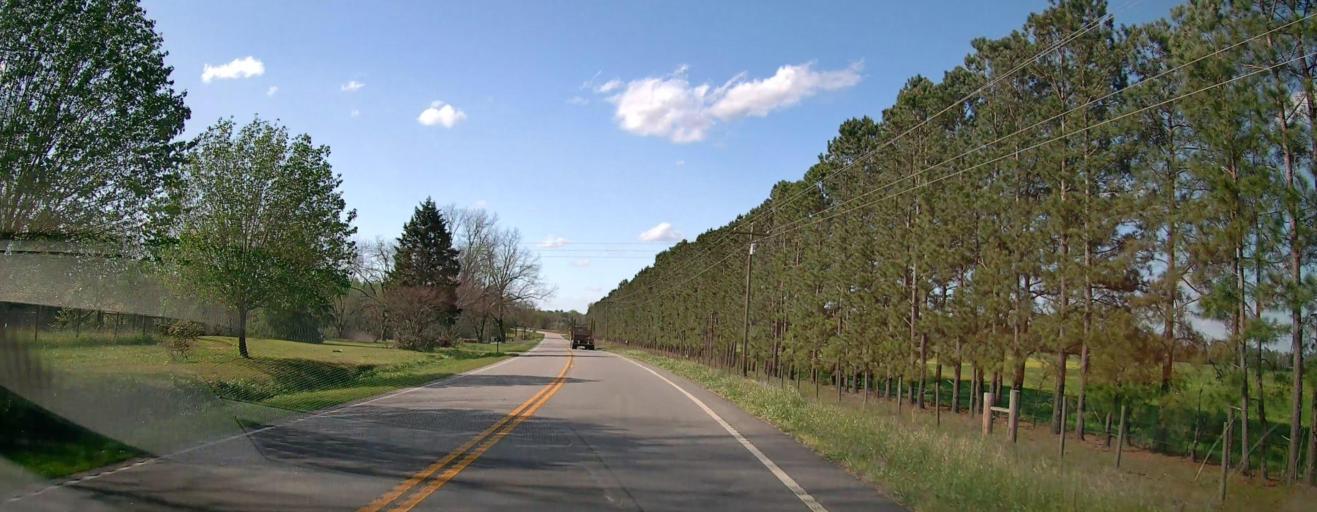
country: US
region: Georgia
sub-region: Baldwin County
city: Hardwick
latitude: 33.0739
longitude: -83.1374
